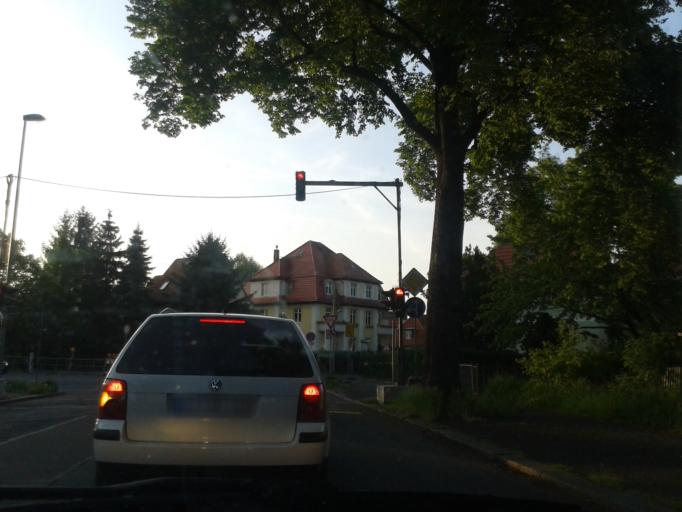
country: DE
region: Saxony
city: Dresden
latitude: 51.0154
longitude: 13.7559
